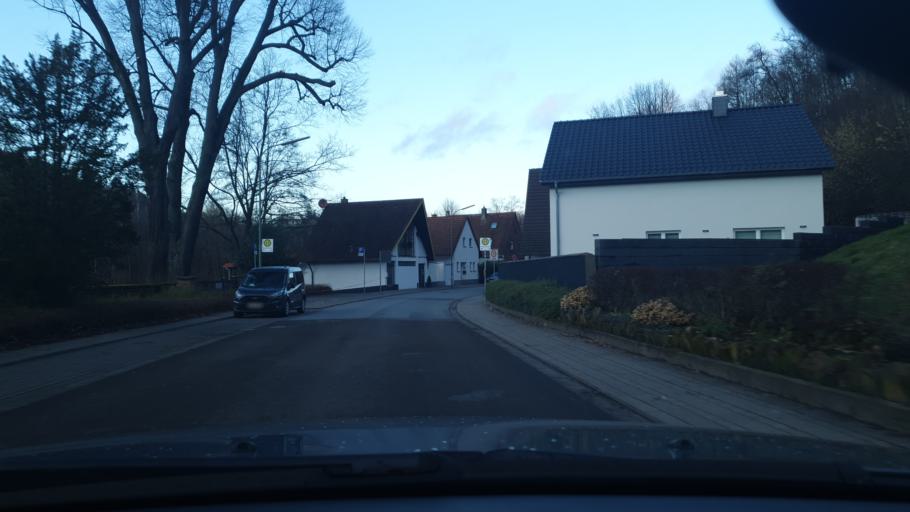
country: DE
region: Rheinland-Pfalz
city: Stelzenberg
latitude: 49.4141
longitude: 7.6979
